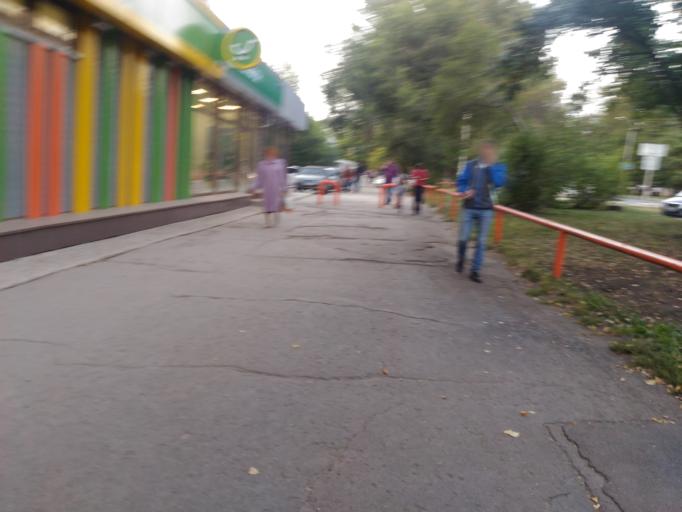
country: RU
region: Ulyanovsk
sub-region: Ulyanovskiy Rayon
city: Ulyanovsk
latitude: 54.3013
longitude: 48.3302
